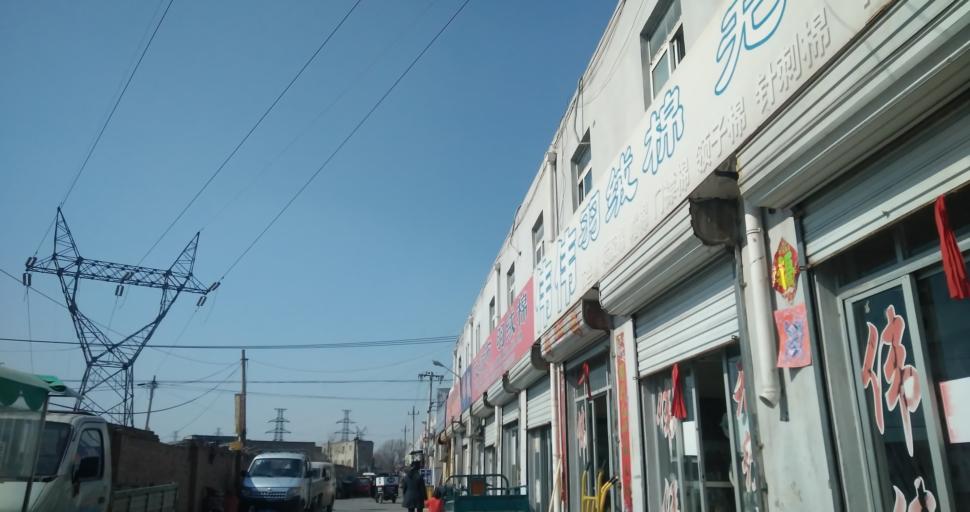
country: CN
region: Beijing
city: Dahongmen
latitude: 39.8211
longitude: 116.4132
